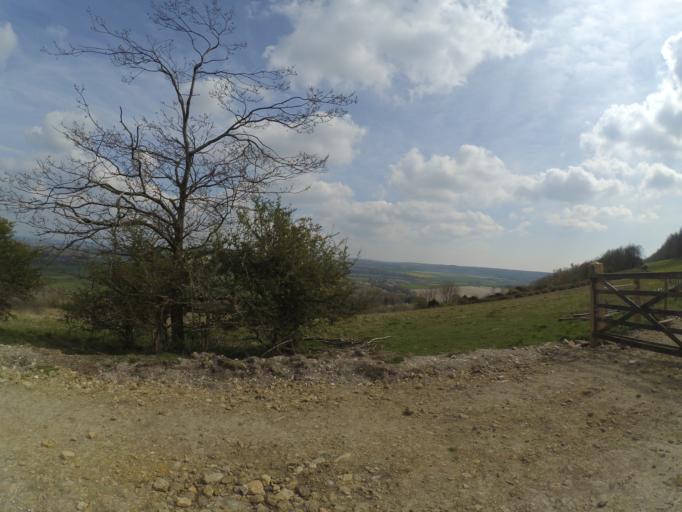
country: GB
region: England
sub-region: West Sussex
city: Arundel
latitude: 50.8796
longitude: -0.5625
